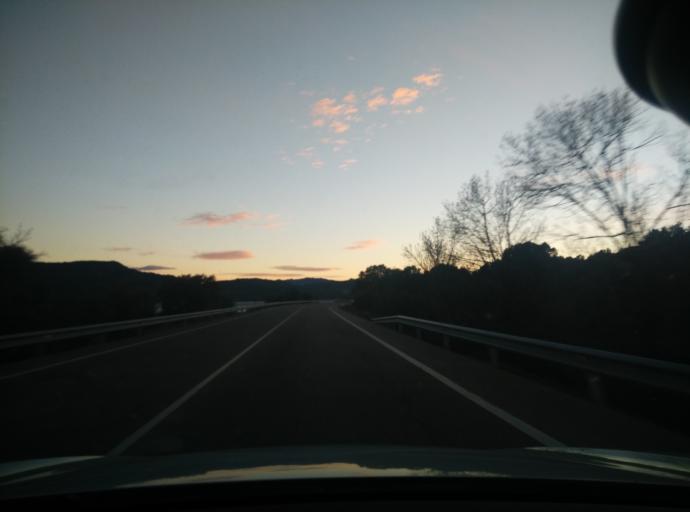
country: ES
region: Madrid
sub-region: Provincia de Madrid
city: Manzanares el Real
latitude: 40.7388
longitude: -3.8436
